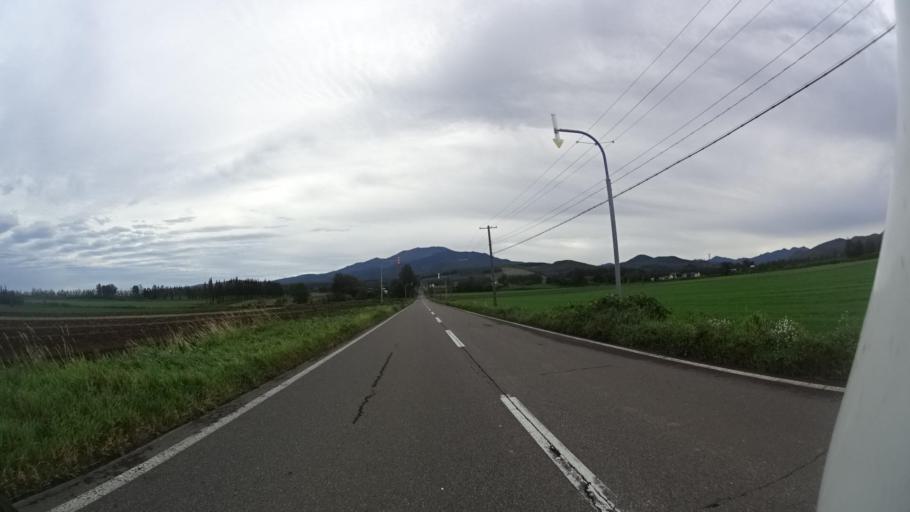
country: JP
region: Hokkaido
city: Shibetsu
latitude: 43.8741
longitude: 144.7403
